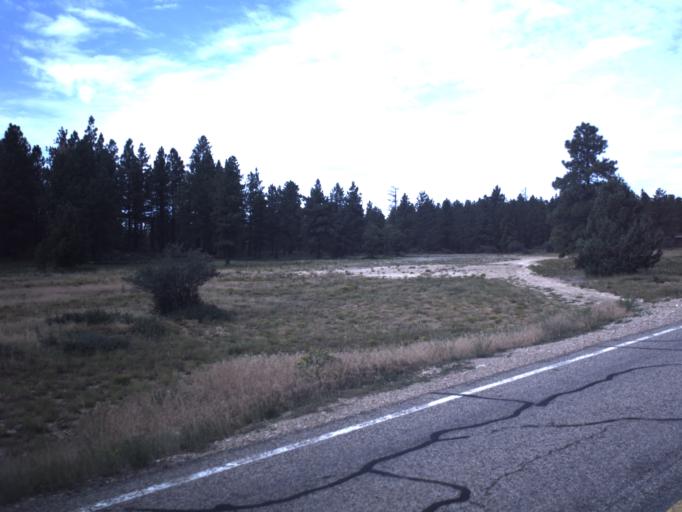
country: US
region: Utah
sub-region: Garfield County
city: Panguitch
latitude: 37.4924
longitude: -112.5615
